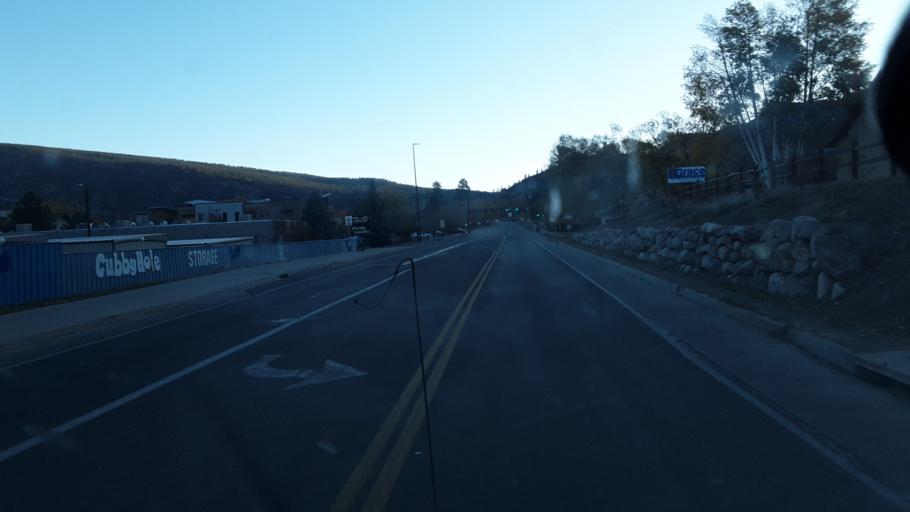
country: US
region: Colorado
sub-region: La Plata County
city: Durango
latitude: 37.2968
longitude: -107.8511
